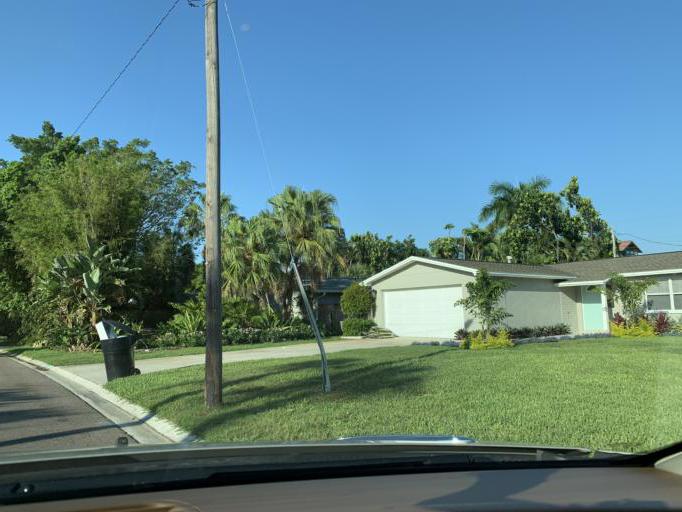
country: US
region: Florida
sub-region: Pinellas County
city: Gandy
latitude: 27.8125
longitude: -82.6034
